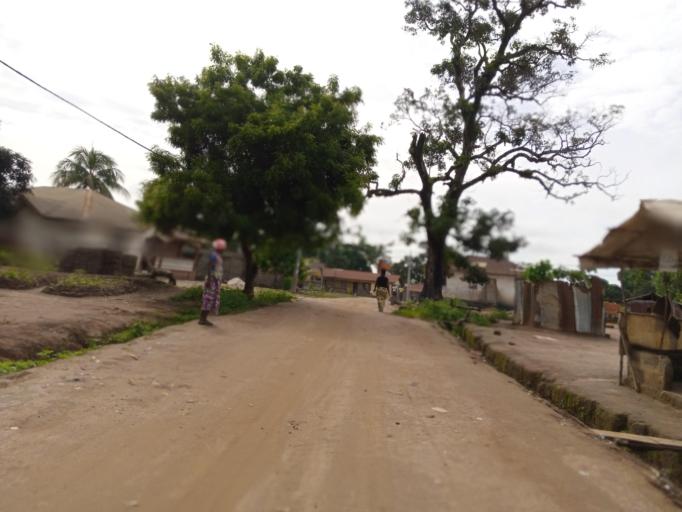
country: SL
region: Northern Province
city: Masoyila
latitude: 8.6074
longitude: -13.1974
